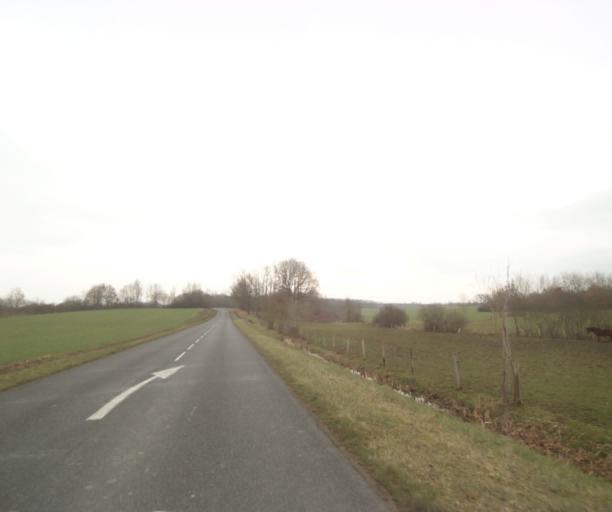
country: FR
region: Champagne-Ardenne
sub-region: Departement de la Marne
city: Pargny-sur-Saulx
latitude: 48.7419
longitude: 4.8508
